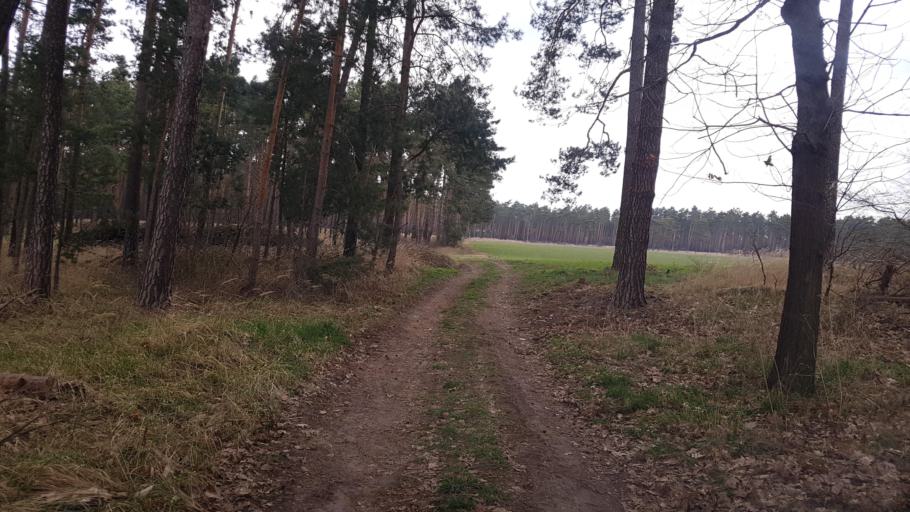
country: DE
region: Brandenburg
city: Finsterwalde
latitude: 51.6133
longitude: 13.6425
